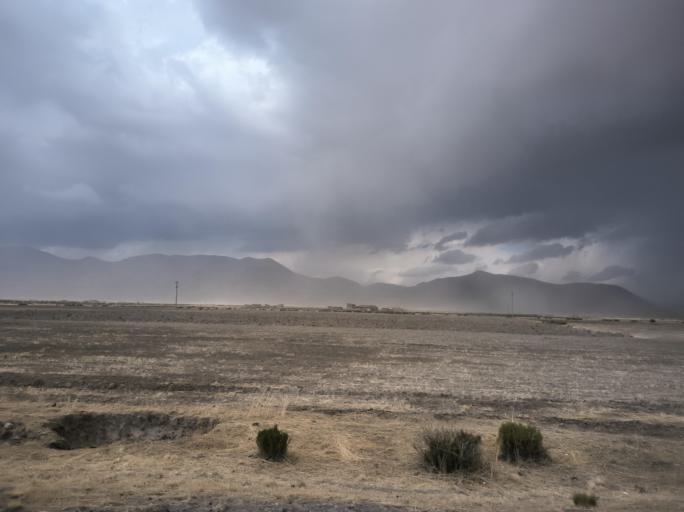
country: BO
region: Oruro
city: Challapata
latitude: -18.7786
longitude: -66.8518
